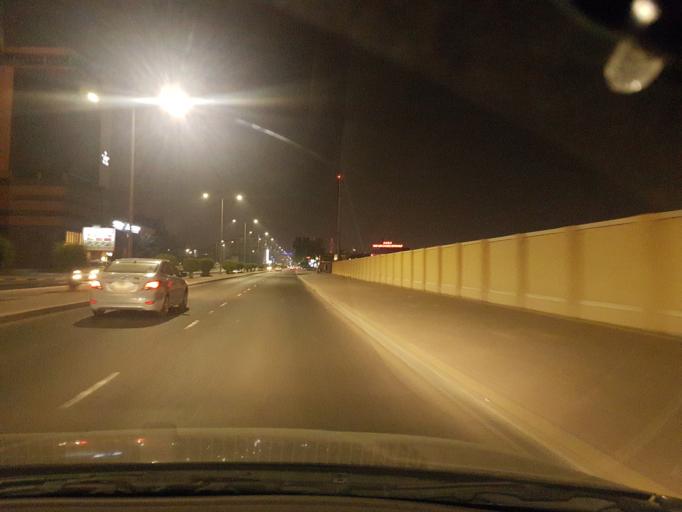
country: BH
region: Manama
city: Manama
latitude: 26.2090
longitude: 50.5943
